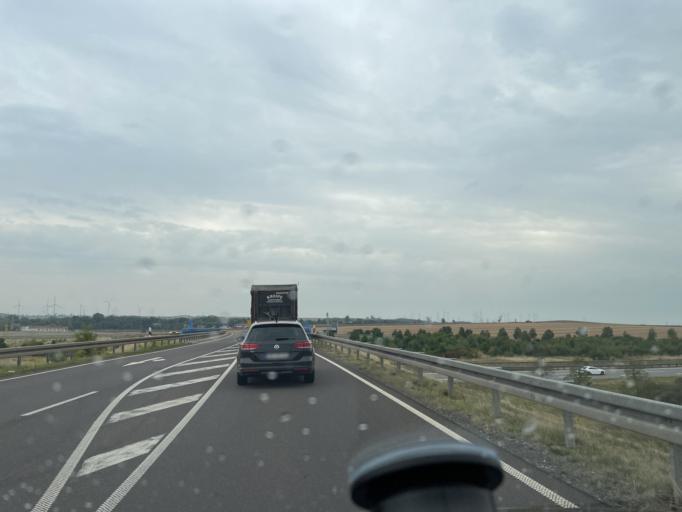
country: DE
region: Saxony-Anhalt
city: Giersleben
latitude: 51.7882
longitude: 11.5697
